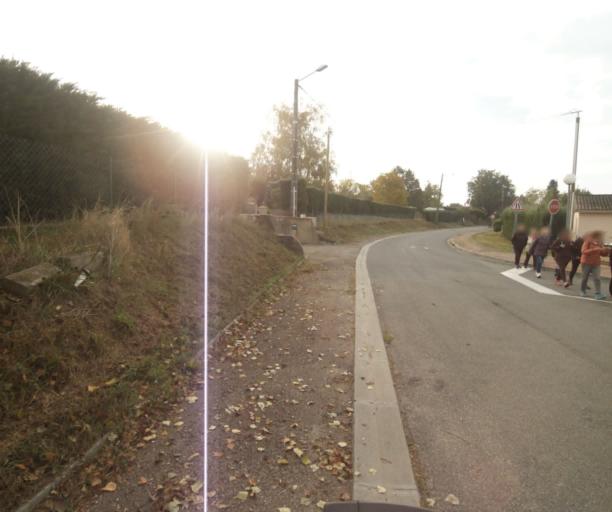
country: FR
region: Midi-Pyrenees
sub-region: Departement du Tarn-et-Garonne
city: Montech
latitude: 43.9658
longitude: 1.2255
